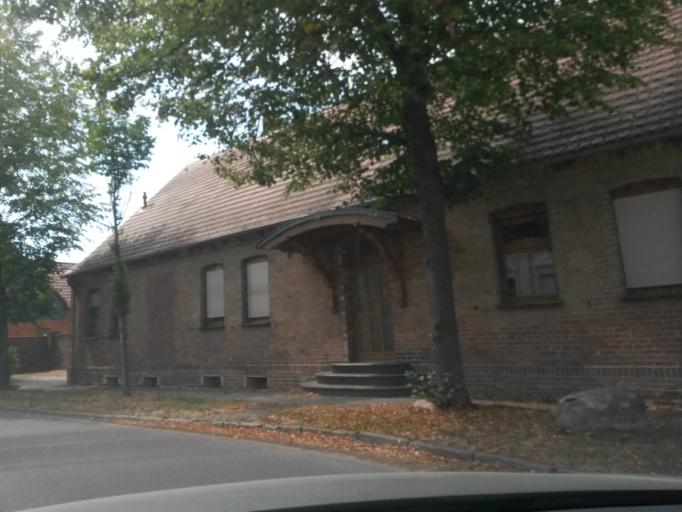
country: DE
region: Saxony-Anhalt
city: Jerichow
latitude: 52.4701
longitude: 12.0207
